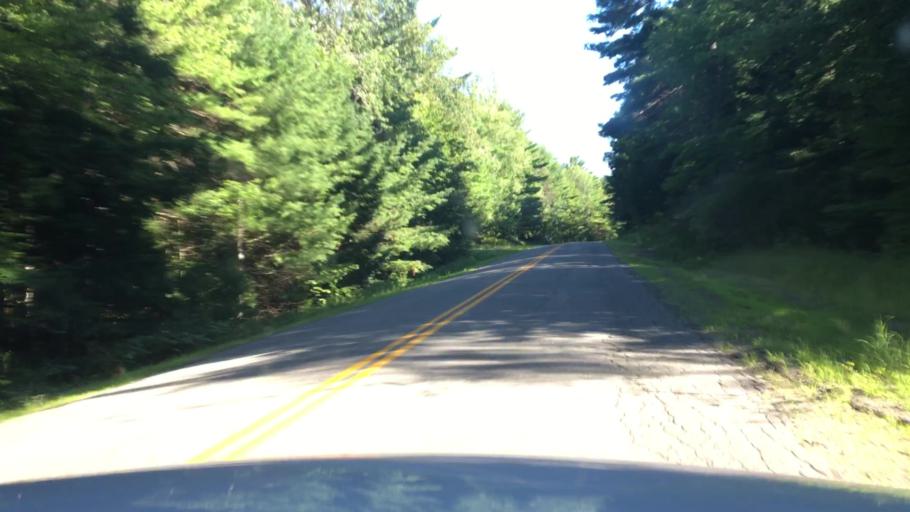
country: US
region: Maine
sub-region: Penobscot County
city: Enfield
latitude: 45.2243
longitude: -68.5801
